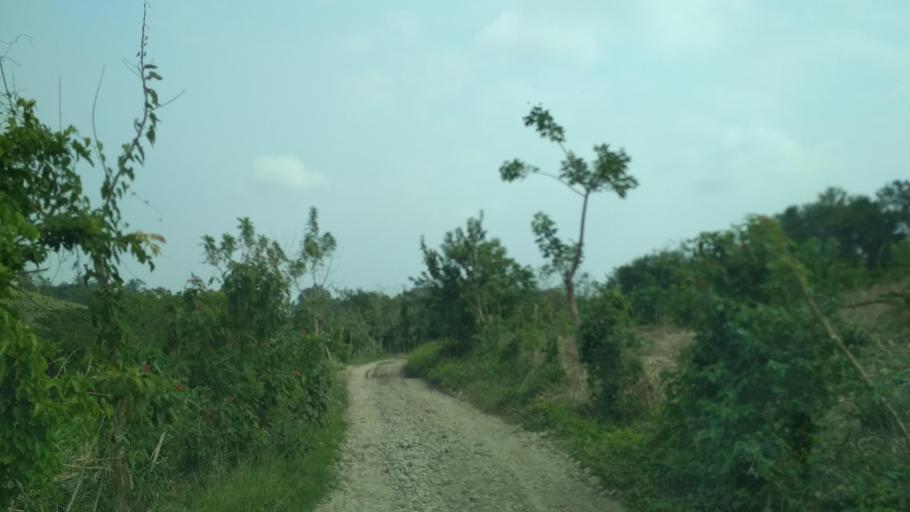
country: MM
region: Kayah
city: Loikaw
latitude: 20.2135
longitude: 97.3148
